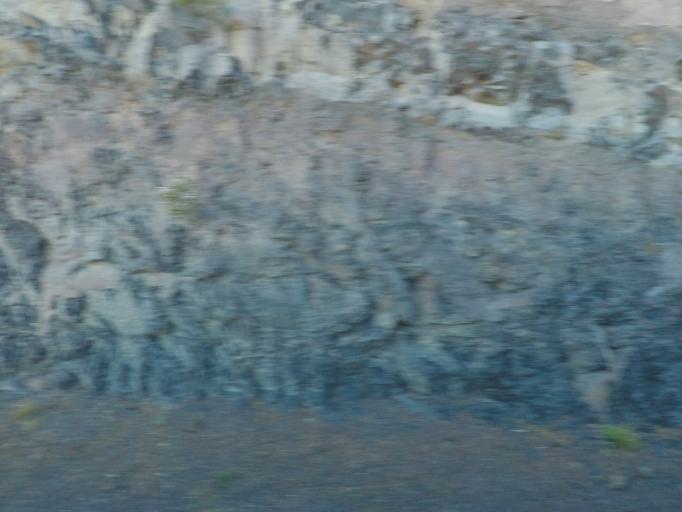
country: ES
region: Canary Islands
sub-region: Provincia de Santa Cruz de Tenerife
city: San Sebastian de la Gomera
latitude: 28.0858
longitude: -17.1287
